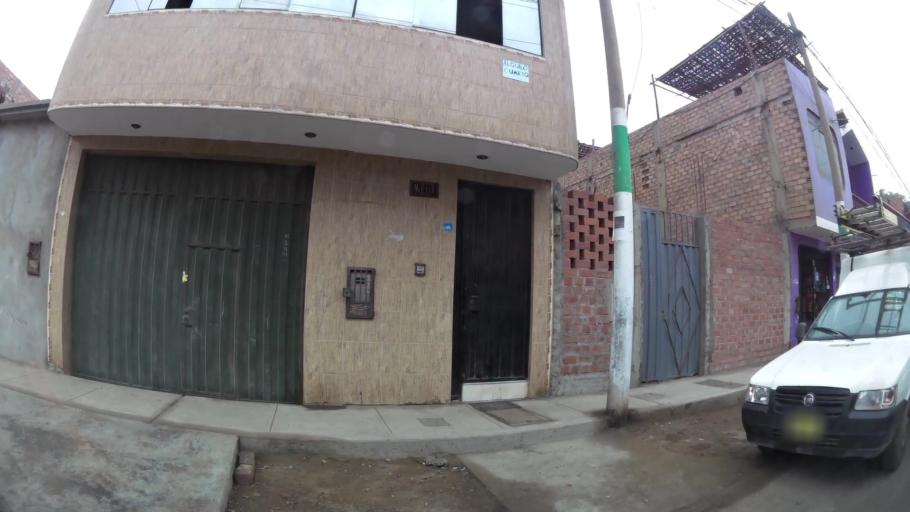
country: PE
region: Lima
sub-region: Lima
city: Urb. Santo Domingo
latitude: -11.8719
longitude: -77.0712
